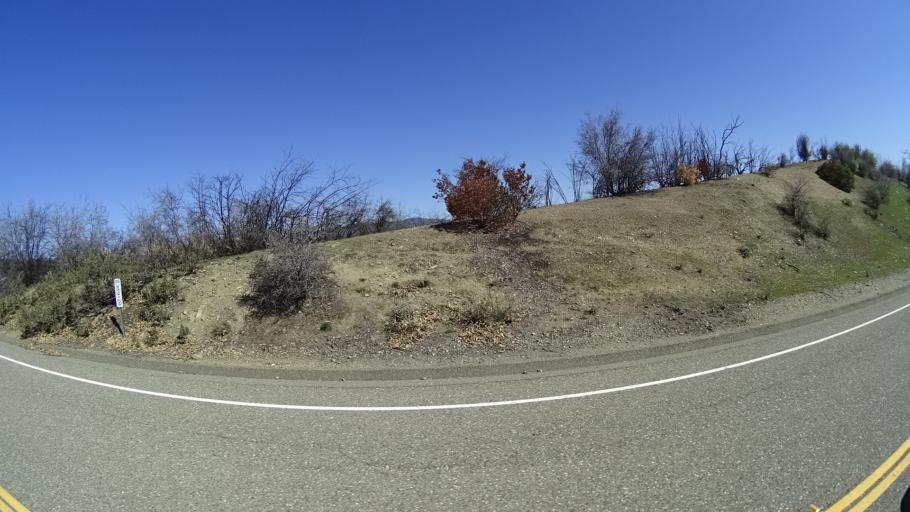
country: US
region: California
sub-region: Tehama County
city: Rancho Tehama Reserve
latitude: 39.6675
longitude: -122.6839
